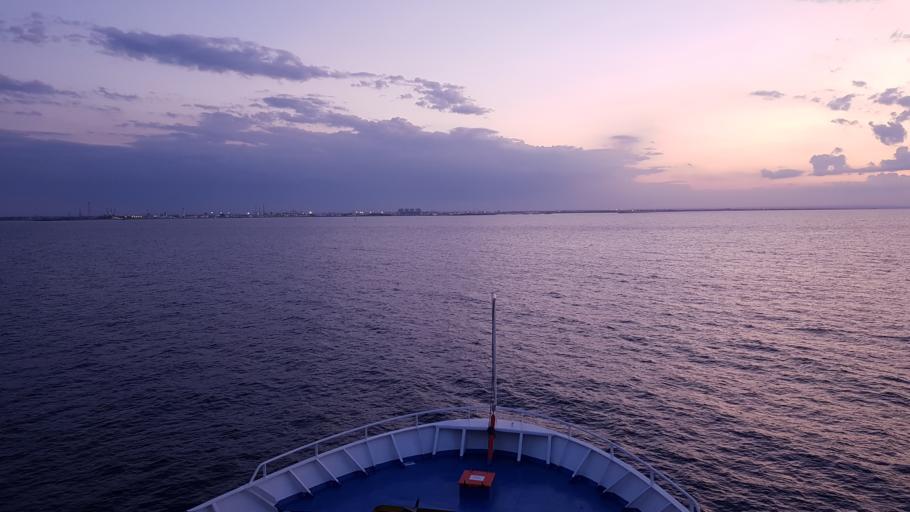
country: IT
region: Apulia
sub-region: Provincia di Brindisi
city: Materdomini
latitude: 40.6679
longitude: 18.0519
